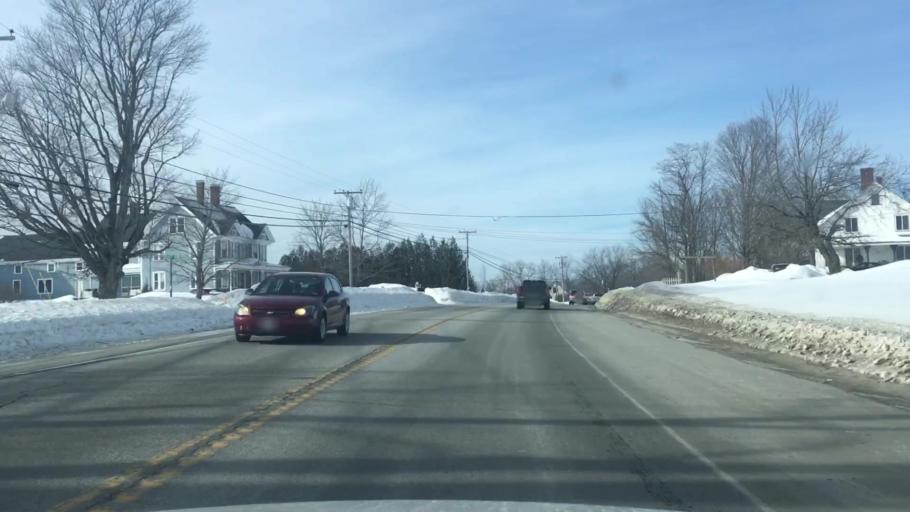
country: US
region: Maine
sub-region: Penobscot County
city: Charleston
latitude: 44.9924
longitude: -69.0181
